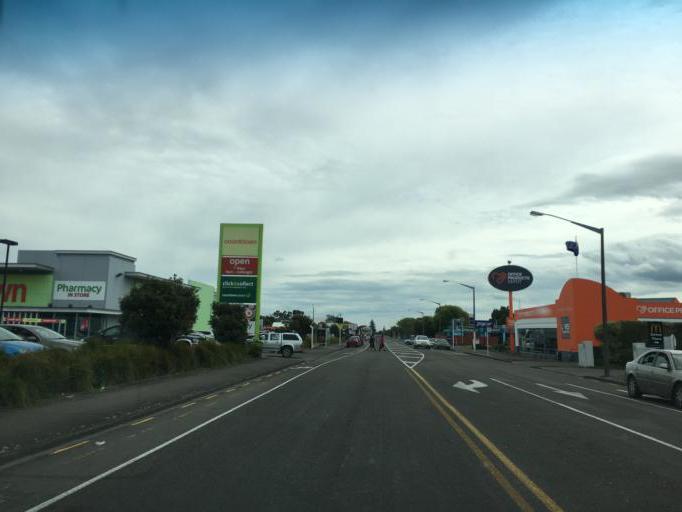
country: NZ
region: Manawatu-Wanganui
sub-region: Palmerston North City
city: Palmerston North
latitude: -40.3500
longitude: 175.6061
